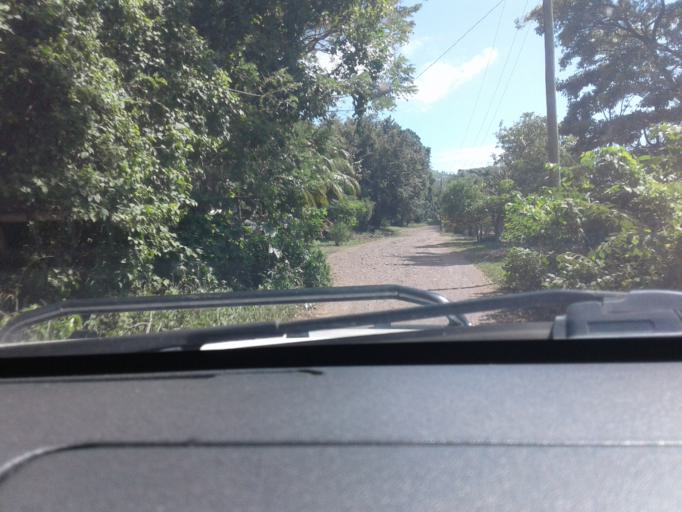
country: NI
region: Rivas
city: Altagracia
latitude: 11.4269
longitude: -85.5492
